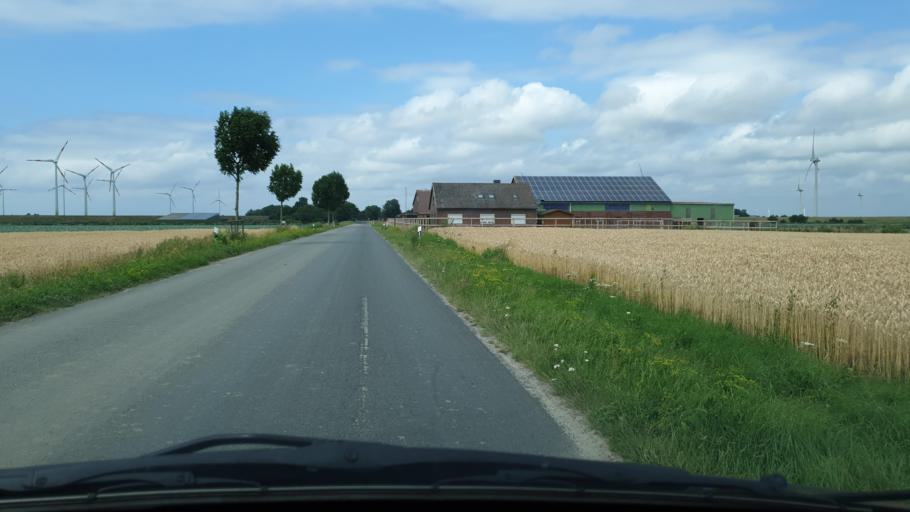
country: DE
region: Schleswig-Holstein
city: Kronprinzenkoog
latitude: 53.9492
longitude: 8.9391
